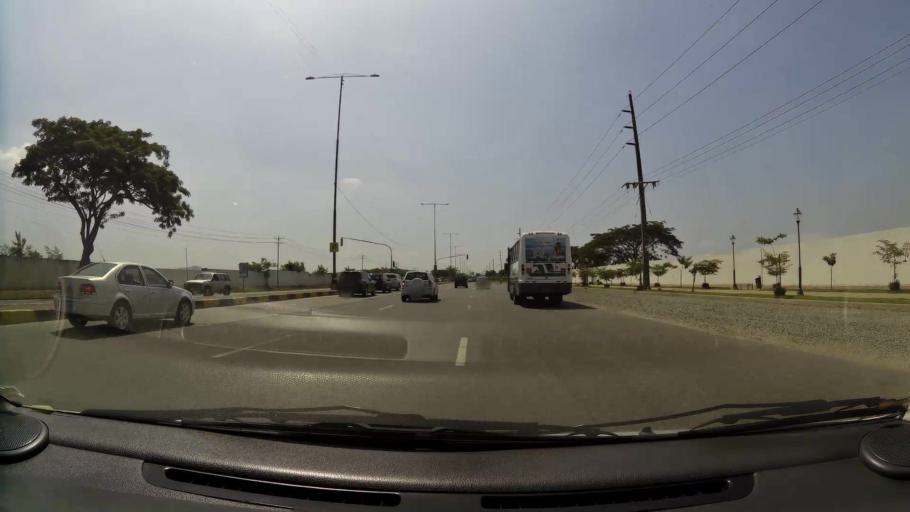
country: EC
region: Guayas
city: Eloy Alfaro
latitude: -2.0717
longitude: -79.8734
